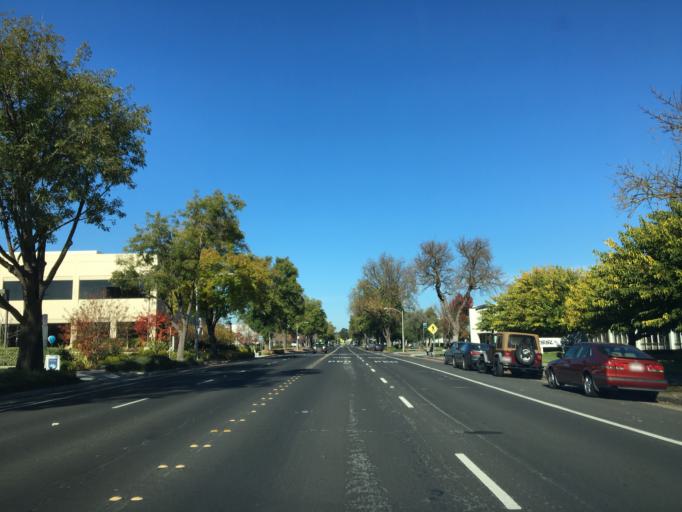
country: US
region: California
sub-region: Santa Clara County
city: Los Altos
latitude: 37.4250
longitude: -122.1042
